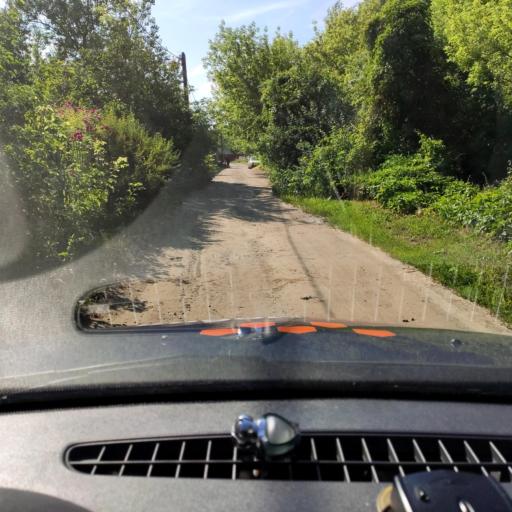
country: RU
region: Voronezj
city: Strelitsa
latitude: 51.6107
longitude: 38.8921
